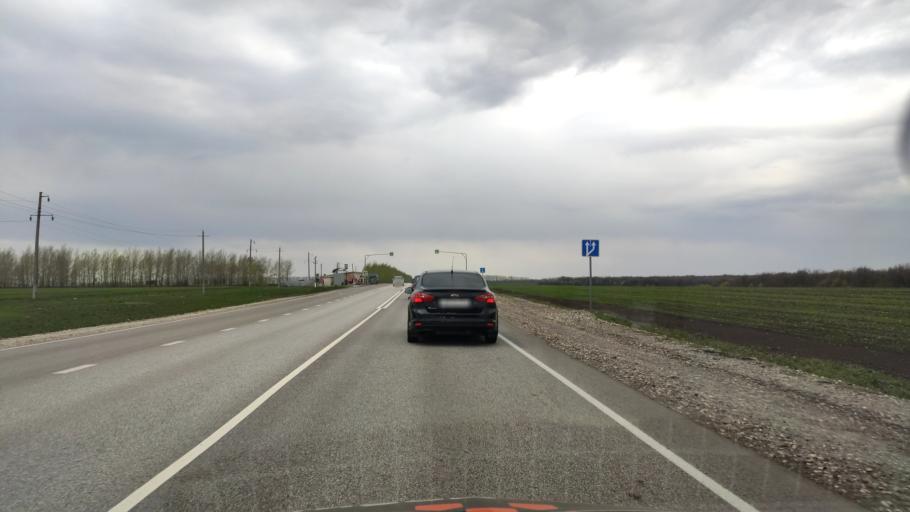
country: RU
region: Voronezj
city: Nizhnedevitsk
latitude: 51.5842
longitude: 38.5436
